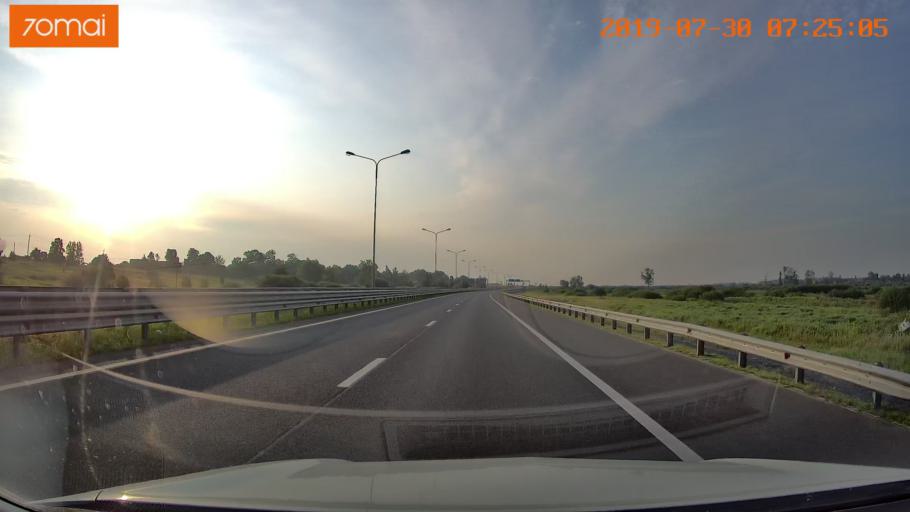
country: RU
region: Kaliningrad
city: Bol'shoe Isakovo
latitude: 54.6890
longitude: 20.8284
